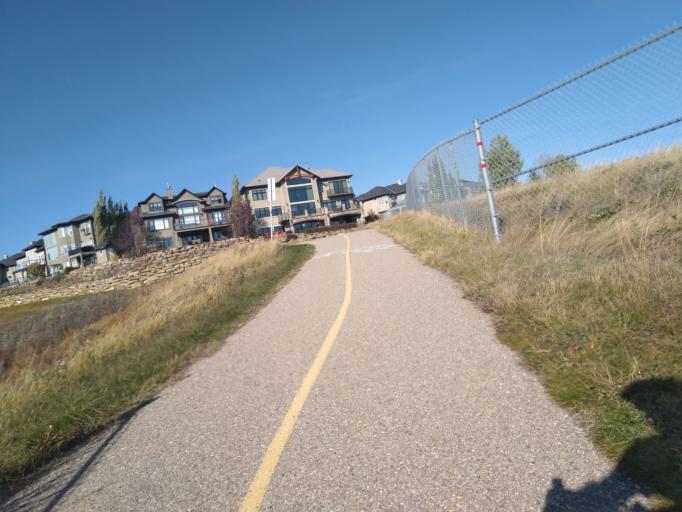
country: CA
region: Alberta
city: Calgary
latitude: 51.1507
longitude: -114.0930
